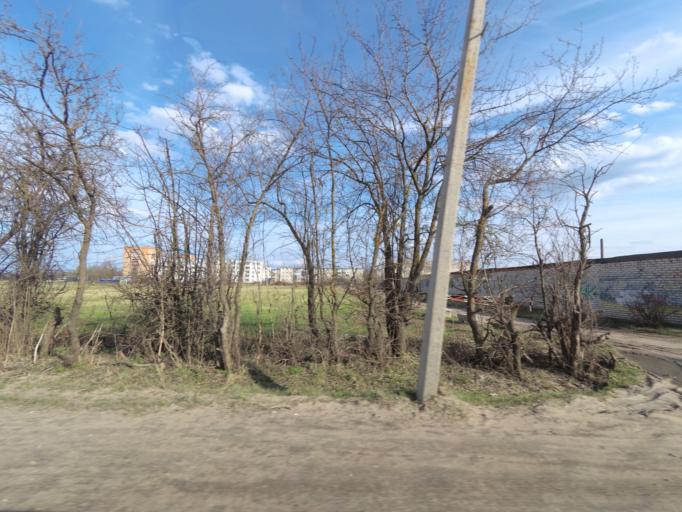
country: RU
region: Moskovskaya
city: Lugovaya
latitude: 56.0462
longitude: 37.4792
